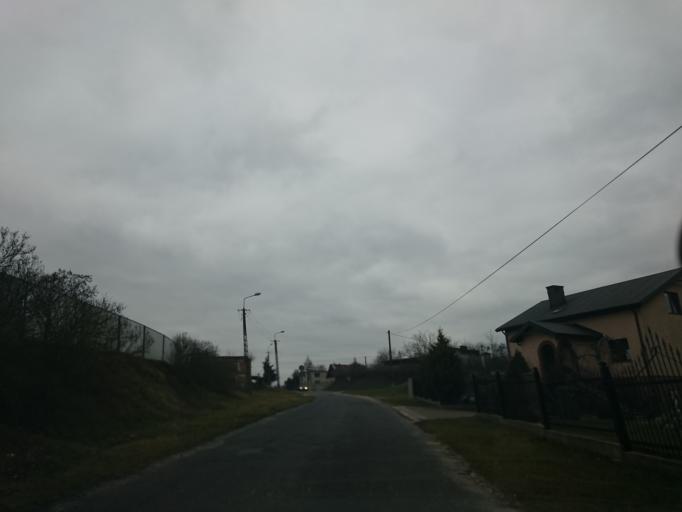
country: PL
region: Kujawsko-Pomorskie
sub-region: Powiat torunski
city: Lubicz Gorny
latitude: 53.0702
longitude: 18.8180
